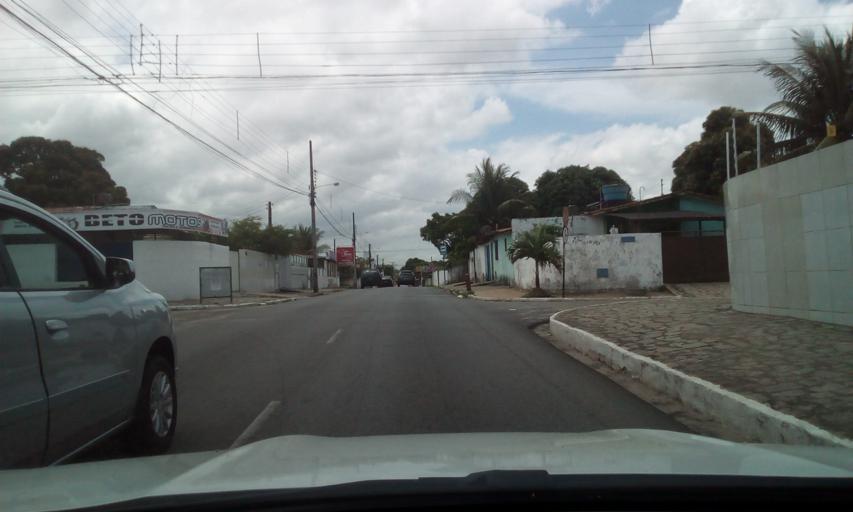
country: BR
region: Paraiba
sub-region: Bayeux
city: Bayeux
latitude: -7.1754
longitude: -34.9156
